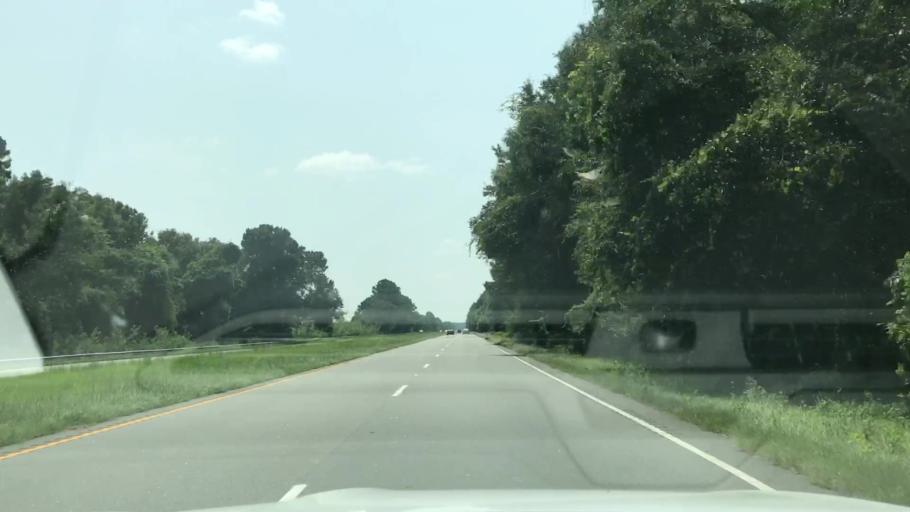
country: US
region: South Carolina
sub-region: Georgetown County
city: Georgetown
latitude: 33.2037
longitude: -79.3890
